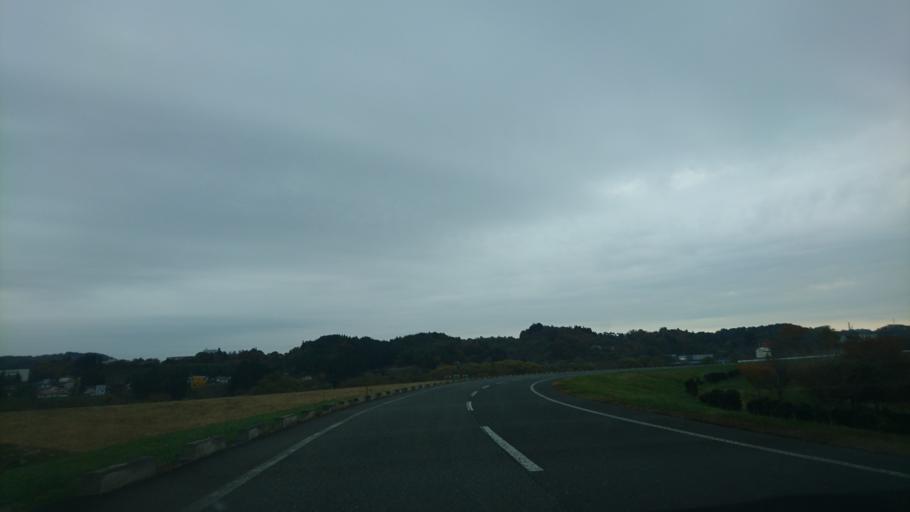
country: JP
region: Iwate
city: Ichinoseki
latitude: 38.9405
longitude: 141.1603
